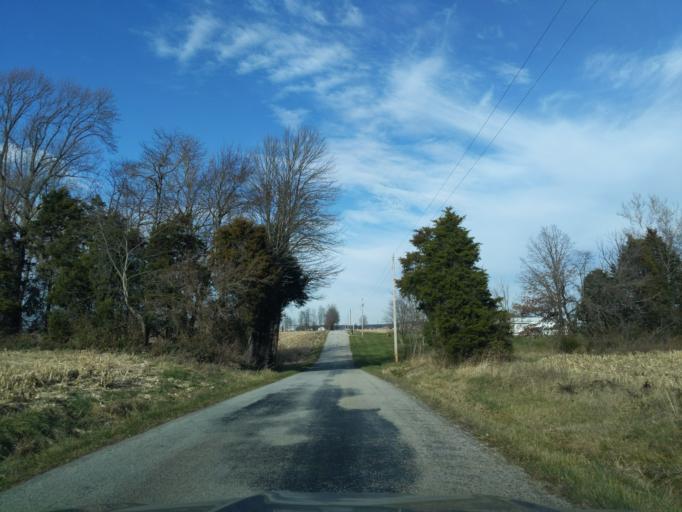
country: US
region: Indiana
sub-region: Decatur County
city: Greensburg
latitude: 39.2375
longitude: -85.4197
